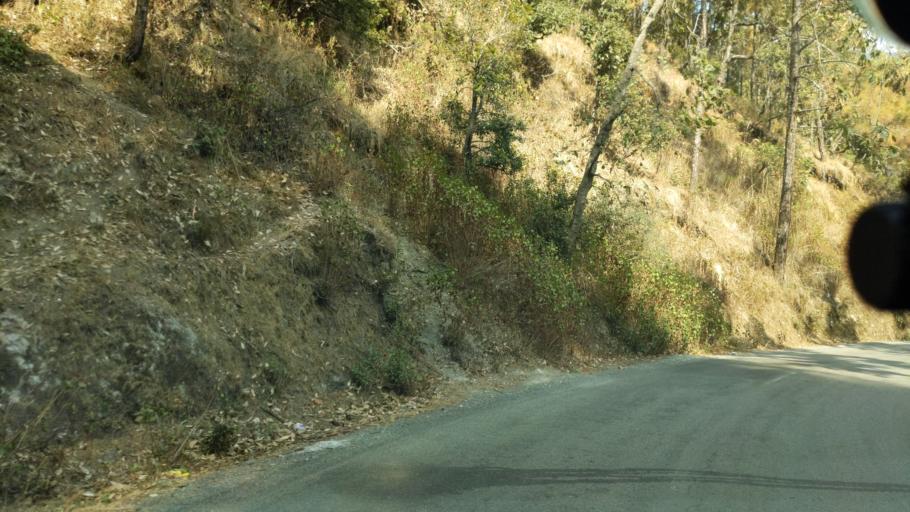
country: IN
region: Uttarakhand
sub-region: Naini Tal
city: Bhowali
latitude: 29.4036
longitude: 79.5367
